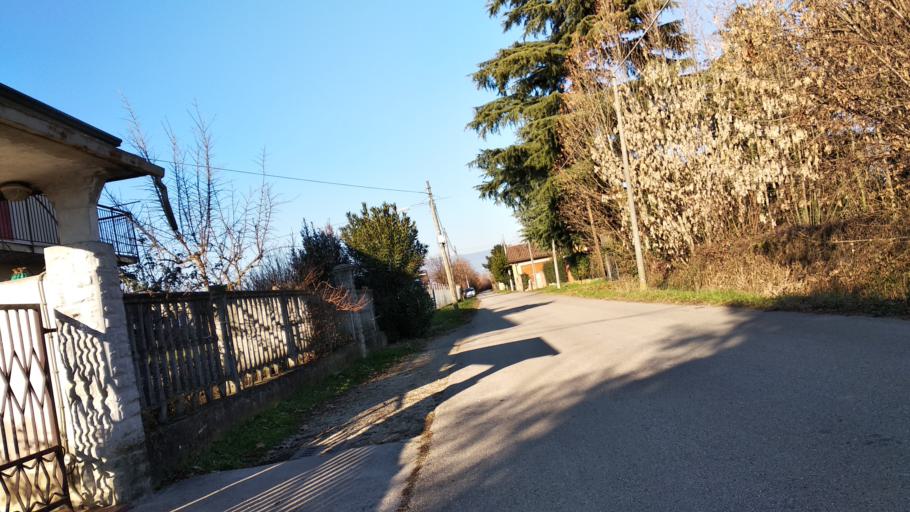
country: IT
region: Veneto
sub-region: Provincia di Vicenza
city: Vicenza
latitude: 45.5770
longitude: 11.5371
